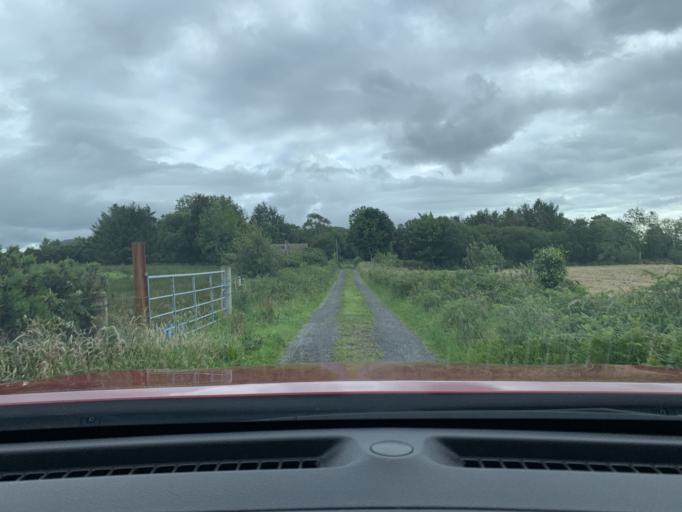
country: IE
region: Connaught
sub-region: County Leitrim
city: Kinlough
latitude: 54.4575
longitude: -8.3572
